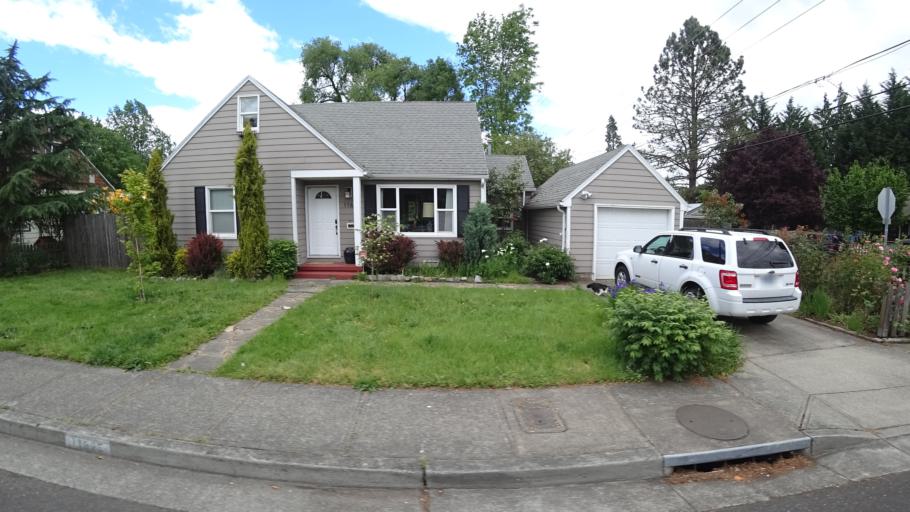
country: US
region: Oregon
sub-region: Washington County
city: Beaverton
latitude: 45.4786
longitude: -122.7968
